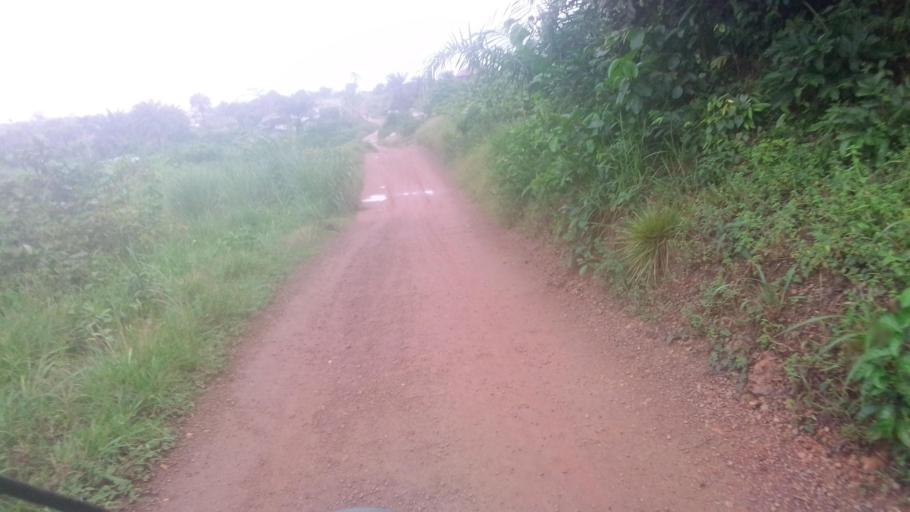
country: SL
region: Eastern Province
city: Kenema
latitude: 7.8314
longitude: -11.2121
